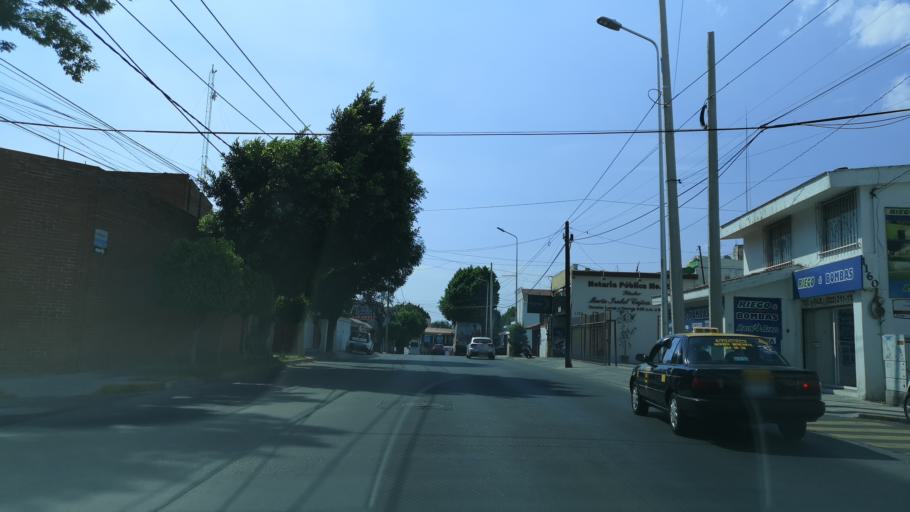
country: MX
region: Puebla
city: Puebla
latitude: 19.0298
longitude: -98.2213
